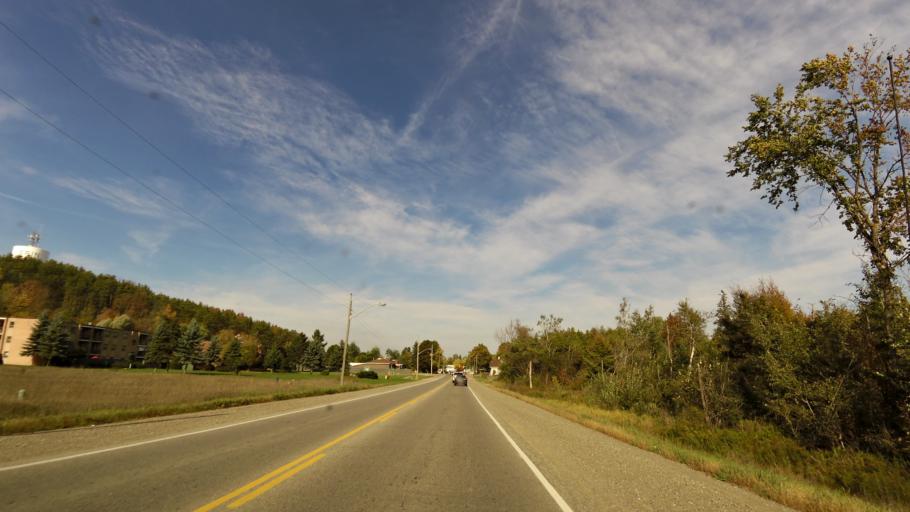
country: CA
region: Ontario
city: Orangeville
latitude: 43.7628
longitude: -80.0599
